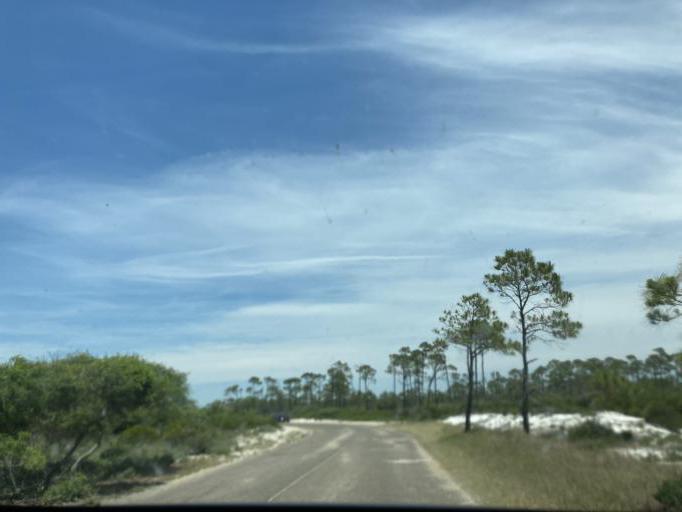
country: US
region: Florida
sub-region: Bay County
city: Lower Grand Lagoon
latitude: 30.1294
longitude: -85.7380
